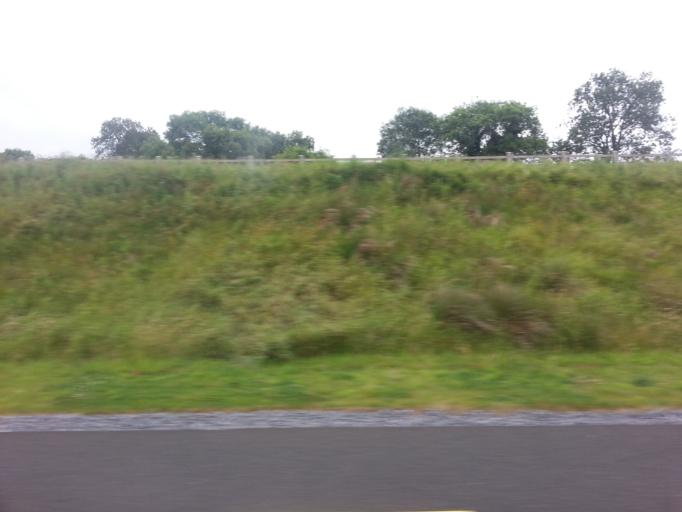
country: IE
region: Leinster
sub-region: Kilkenny
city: Kilkenny
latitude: 52.6506
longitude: -7.1938
